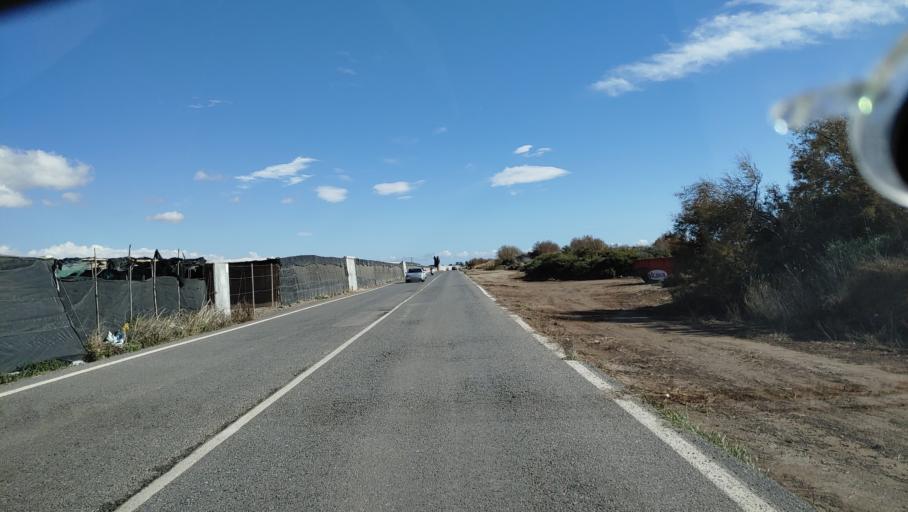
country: ES
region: Andalusia
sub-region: Provincia de Almeria
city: Roquetas de Mar
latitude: 36.7896
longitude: -2.5993
